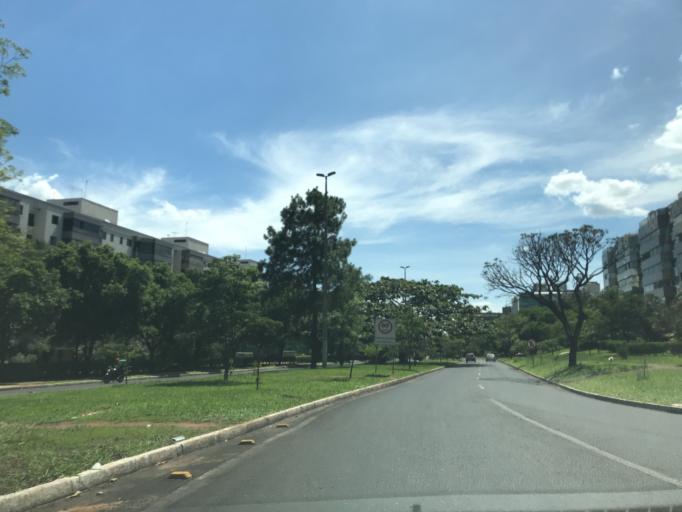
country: BR
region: Federal District
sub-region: Brasilia
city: Brasilia
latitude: -15.8038
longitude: -47.9307
